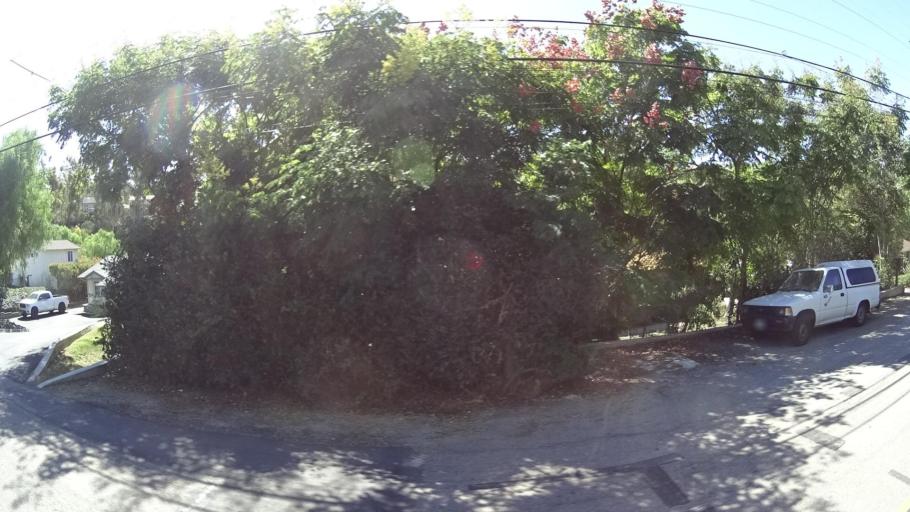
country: US
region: California
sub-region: San Diego County
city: Bonita
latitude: 32.6588
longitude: -117.0184
